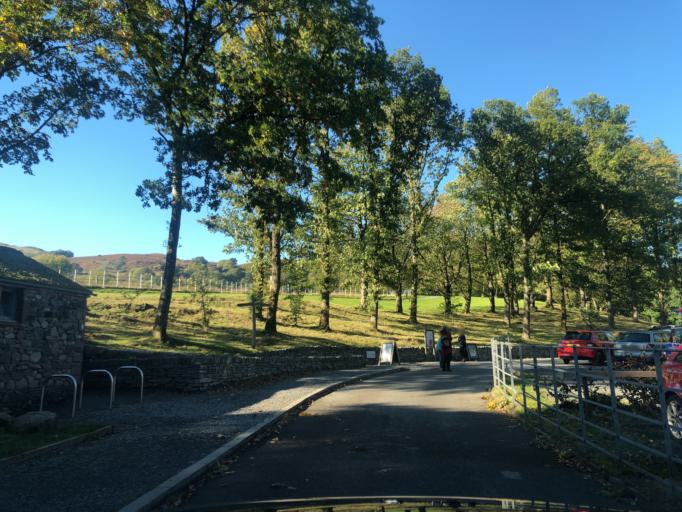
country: GB
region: England
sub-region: Cumbria
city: Ambleside
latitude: 54.5716
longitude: -2.9287
